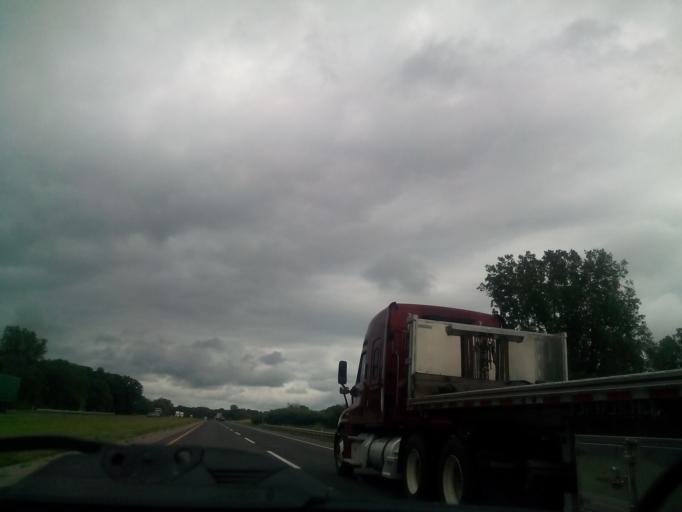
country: US
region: Michigan
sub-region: Branch County
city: Bronson
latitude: 41.7546
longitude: -85.2458
